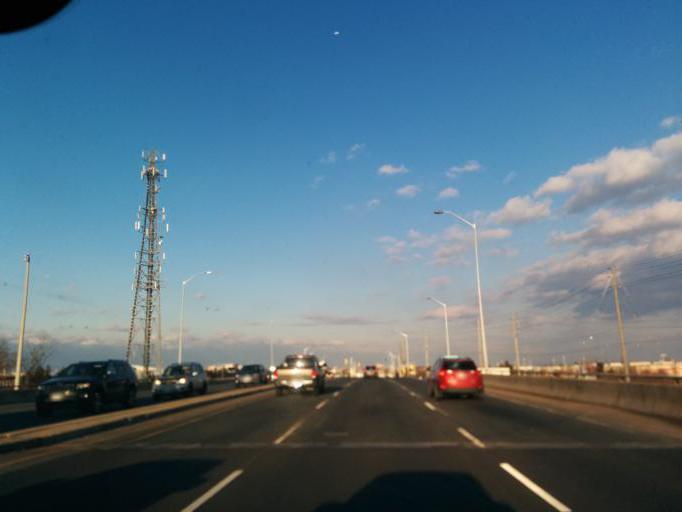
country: CA
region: Ontario
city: Oakville
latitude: 43.5116
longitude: -79.6935
